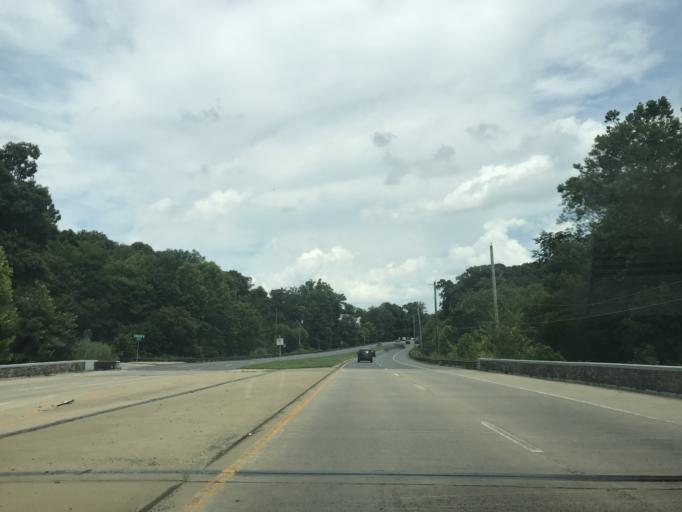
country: US
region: Delaware
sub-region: New Castle County
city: Greenville
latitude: 39.7627
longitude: -75.6365
